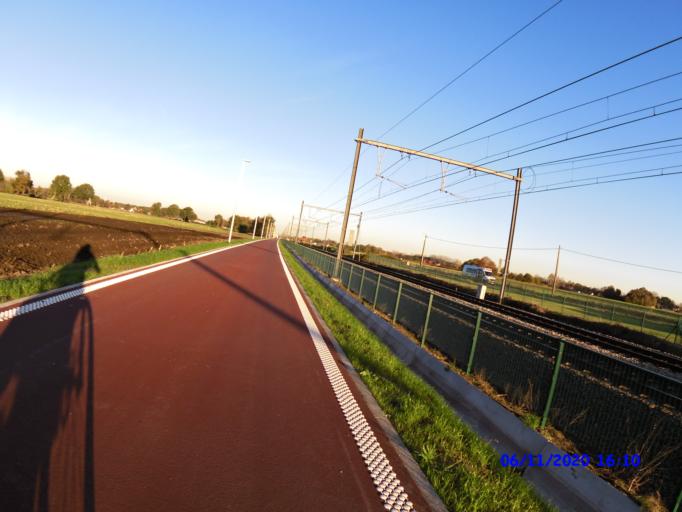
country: BE
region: Flanders
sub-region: Provincie Antwerpen
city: Geel
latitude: 51.1740
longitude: 5.0193
